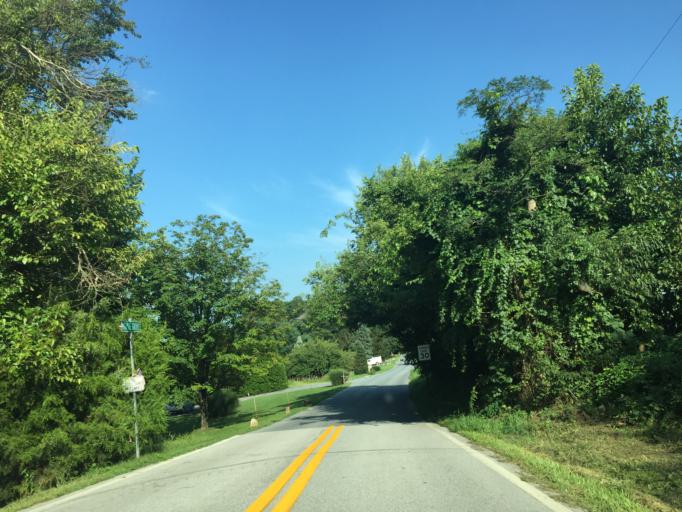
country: US
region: Maryland
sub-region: Carroll County
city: Hampstead
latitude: 39.6452
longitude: -76.8163
